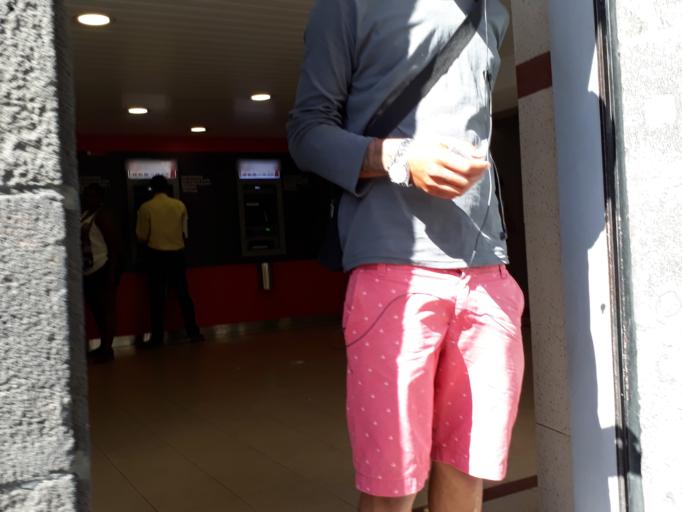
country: MU
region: Port Louis
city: Port Louis
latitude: -20.1630
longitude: 57.4999
